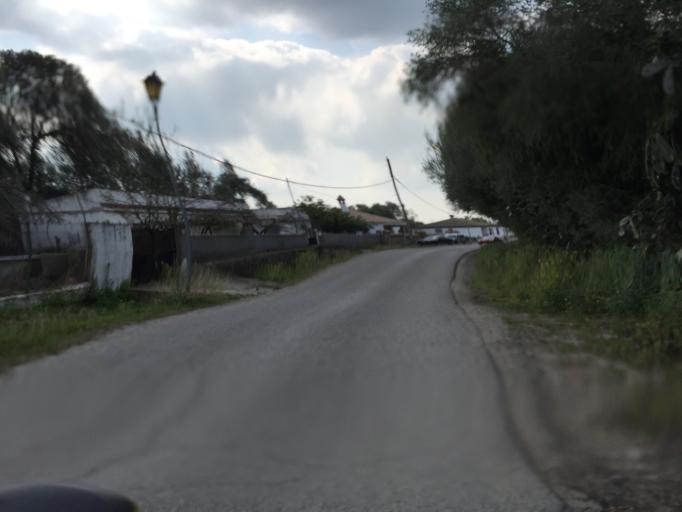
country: ES
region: Andalusia
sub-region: Provincia de Cadiz
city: Benalup-Casas Viejas
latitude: 36.3189
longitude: -5.8843
